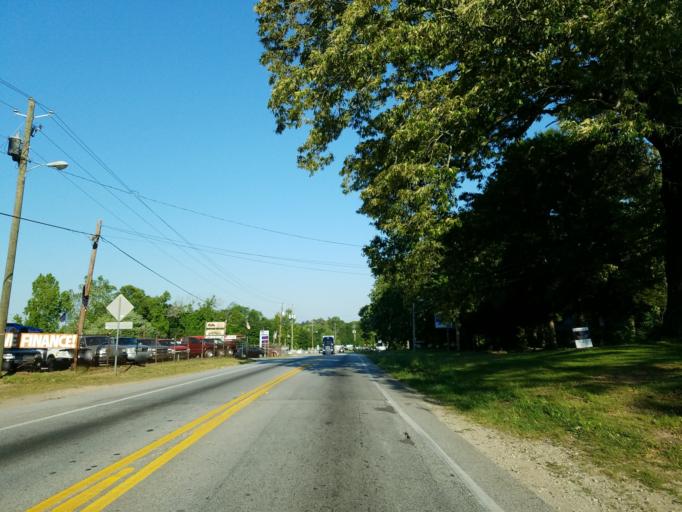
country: US
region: Georgia
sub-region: Douglas County
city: Lithia Springs
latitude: 33.7966
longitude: -84.6501
